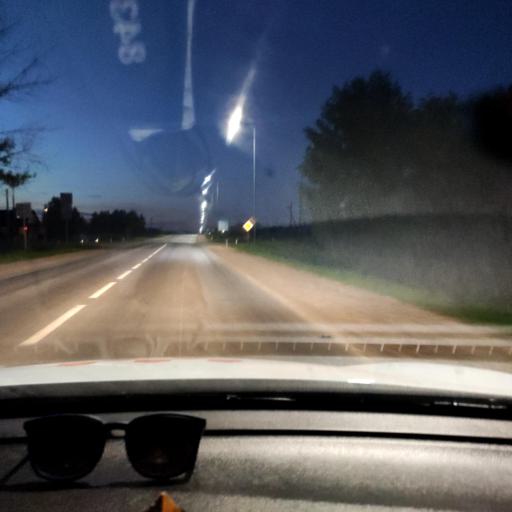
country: RU
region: Tatarstan
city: Rybnaya Sloboda
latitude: 55.4293
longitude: 49.8905
